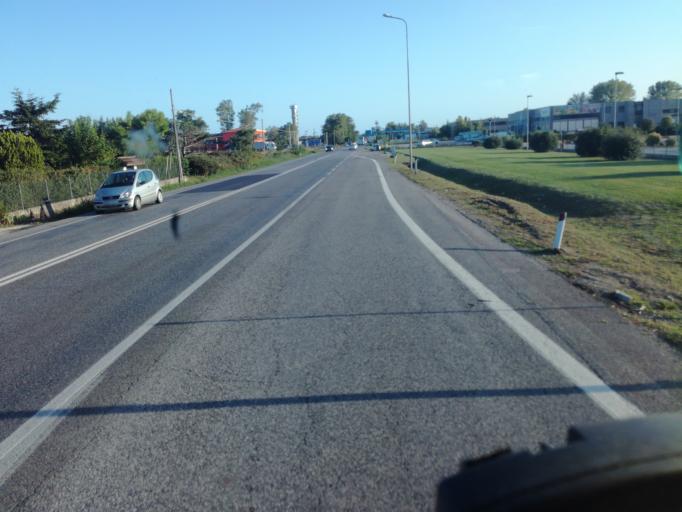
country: IT
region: Emilia-Romagna
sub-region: Provincia di Ferrara
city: Lido di Pomposa-Lido degli Scacchi
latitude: 44.6951
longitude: 12.2226
